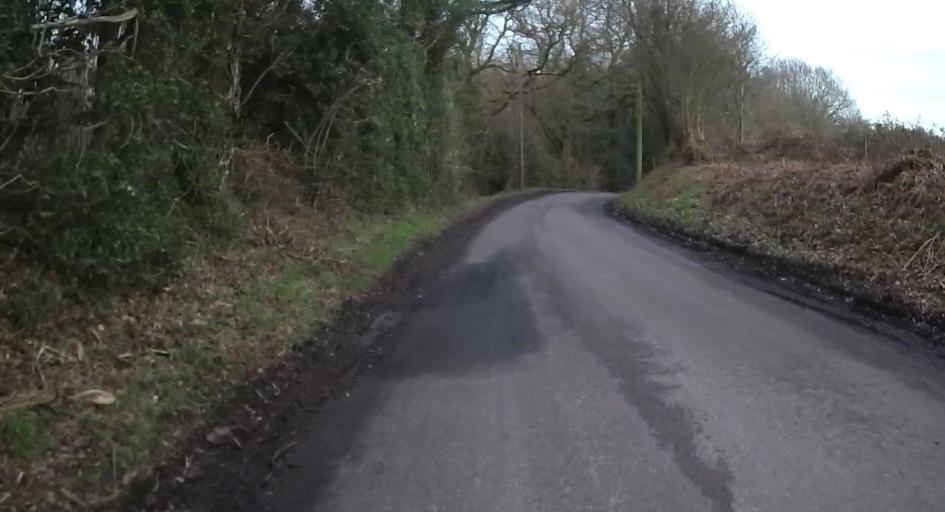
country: GB
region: England
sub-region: West Berkshire
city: Stratfield Mortimer
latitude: 51.3680
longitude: -1.0654
